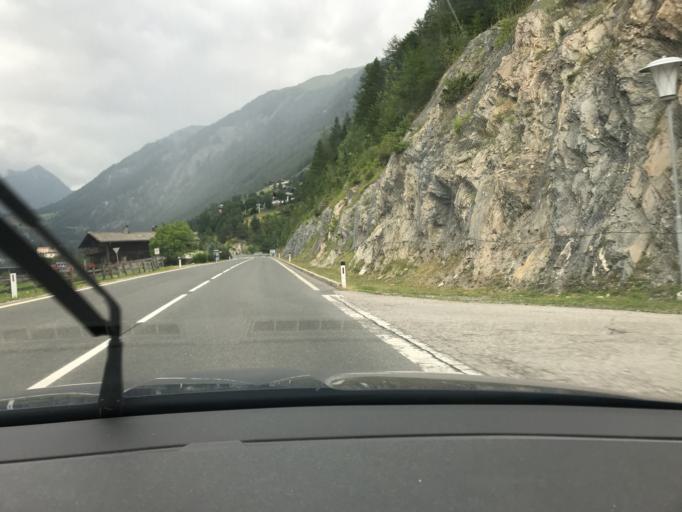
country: AT
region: Tyrol
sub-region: Politischer Bezirk Lienz
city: Matrei in Osttirol
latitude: 47.0008
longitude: 12.5422
